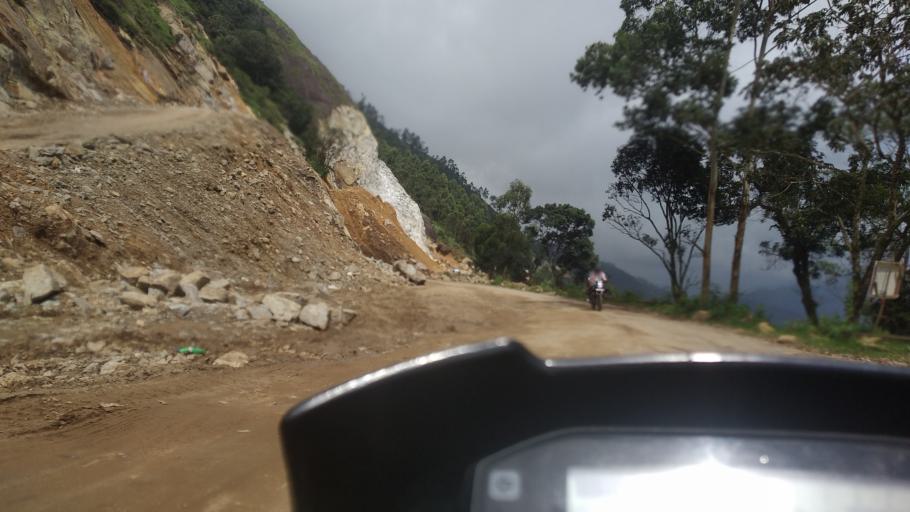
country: IN
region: Kerala
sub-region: Idukki
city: Munnar
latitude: 10.0368
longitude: 77.1285
